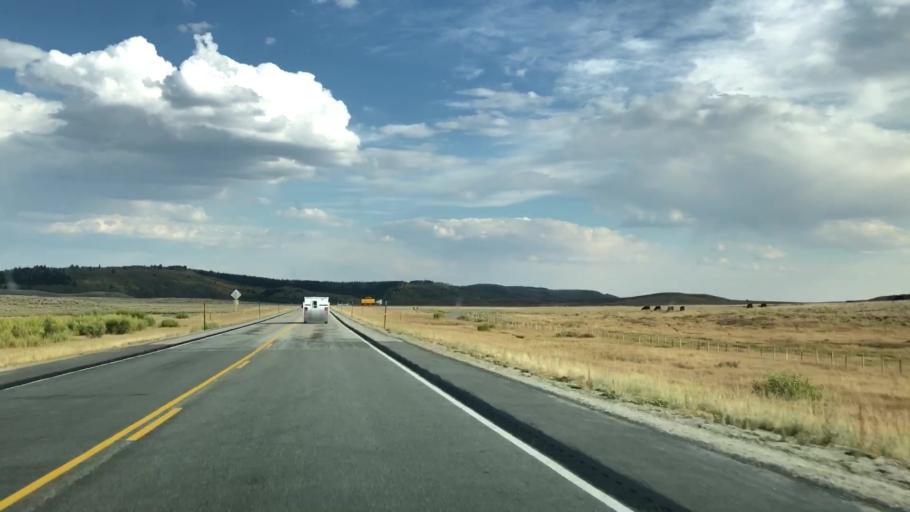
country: US
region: Wyoming
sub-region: Sublette County
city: Pinedale
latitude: 43.1254
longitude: -110.1884
